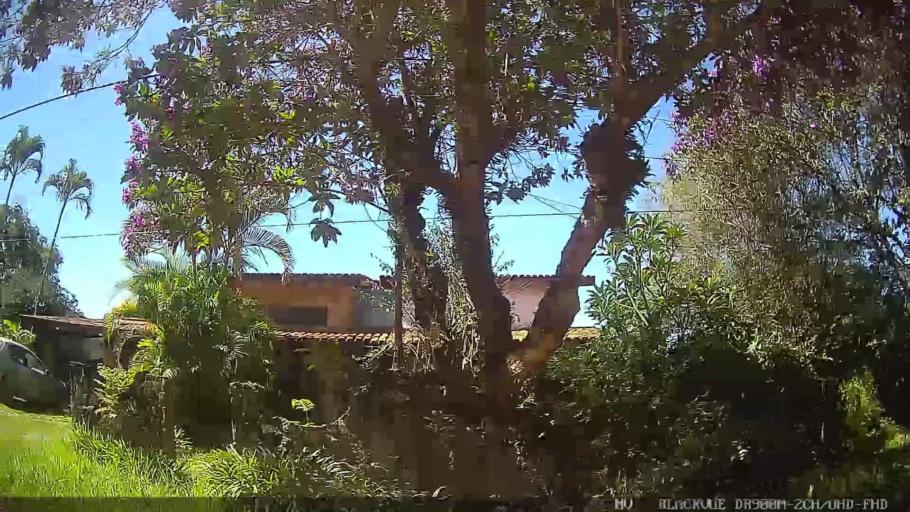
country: BR
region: Sao Paulo
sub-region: Atibaia
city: Atibaia
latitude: -23.1025
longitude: -46.5757
